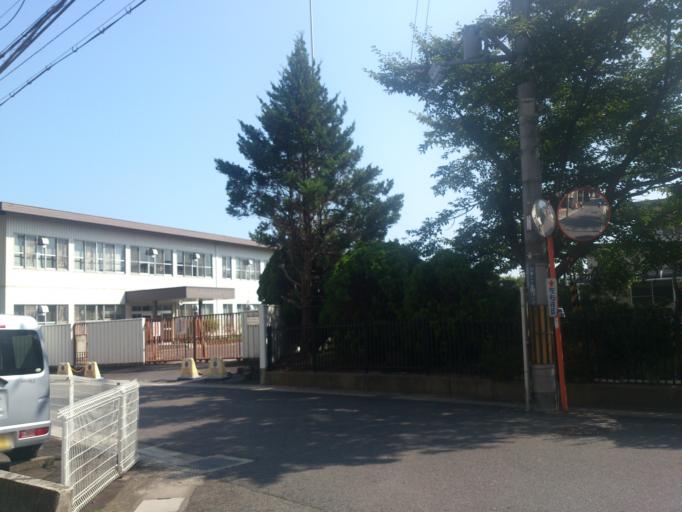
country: JP
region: Shiga Prefecture
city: Kusatsu
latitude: 34.9869
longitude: 135.9270
